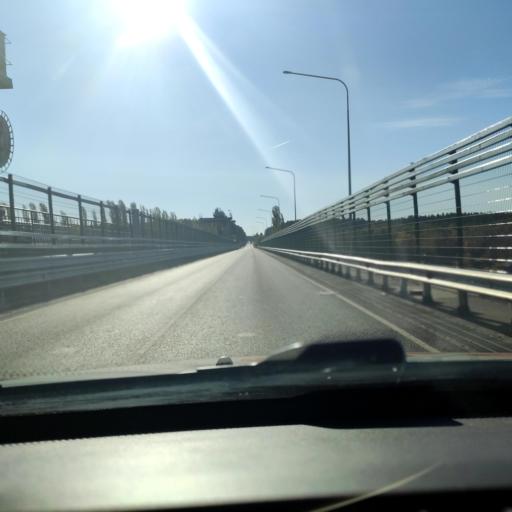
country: RU
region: Voronezj
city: Shilovo
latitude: 51.5395
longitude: 39.1383
